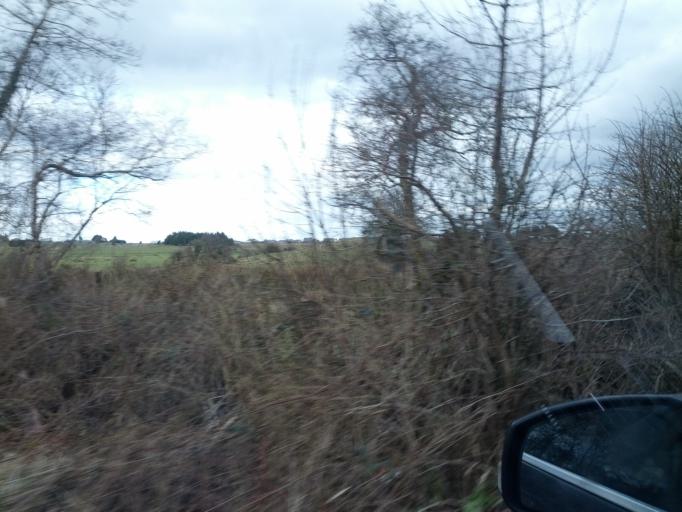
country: IE
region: Connaught
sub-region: County Galway
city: Athenry
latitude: 53.3353
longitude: -8.6900
